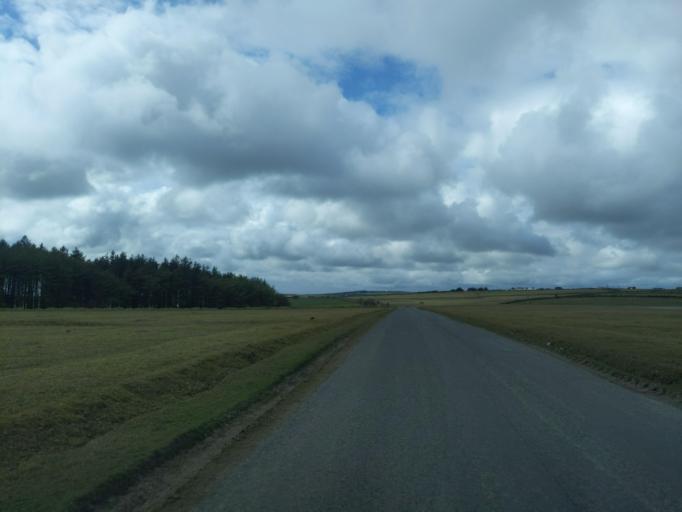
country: GB
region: England
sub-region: Cornwall
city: Camelford
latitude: 50.6392
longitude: -4.6277
